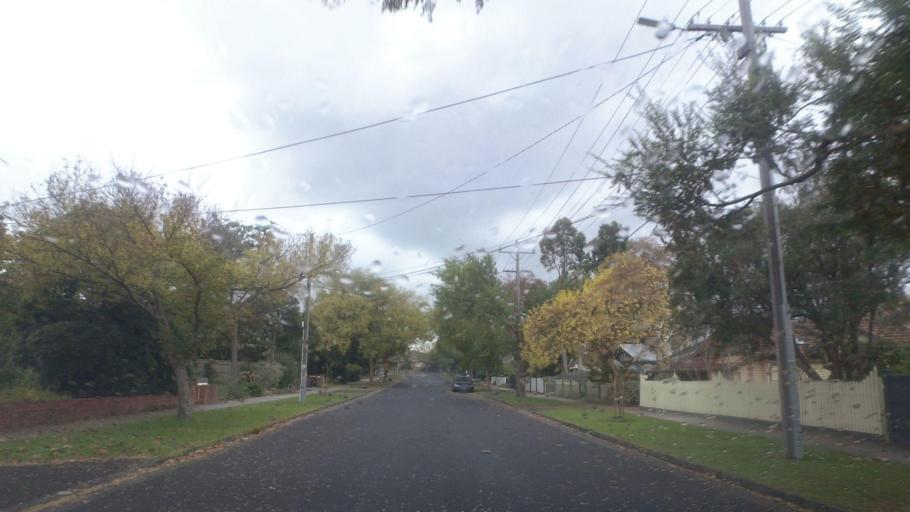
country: AU
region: Victoria
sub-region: Whitehorse
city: Box Hill
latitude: -37.8248
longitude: 145.1317
